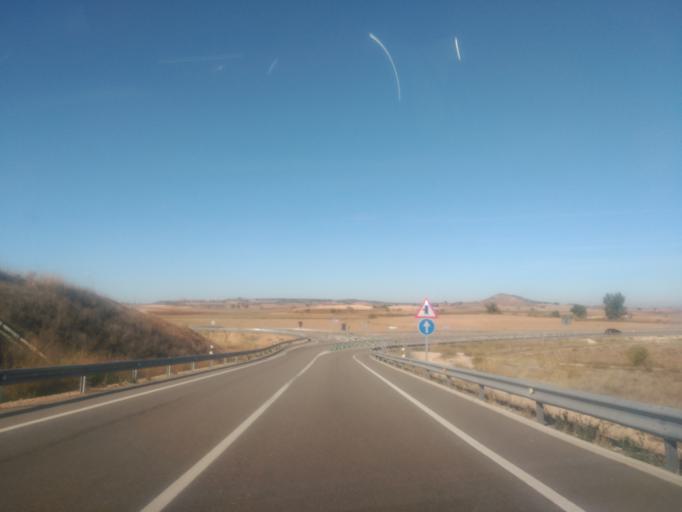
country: ES
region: Castille and Leon
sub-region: Provincia de Burgos
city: Castrillo de la Vega
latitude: 41.6367
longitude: -3.7804
